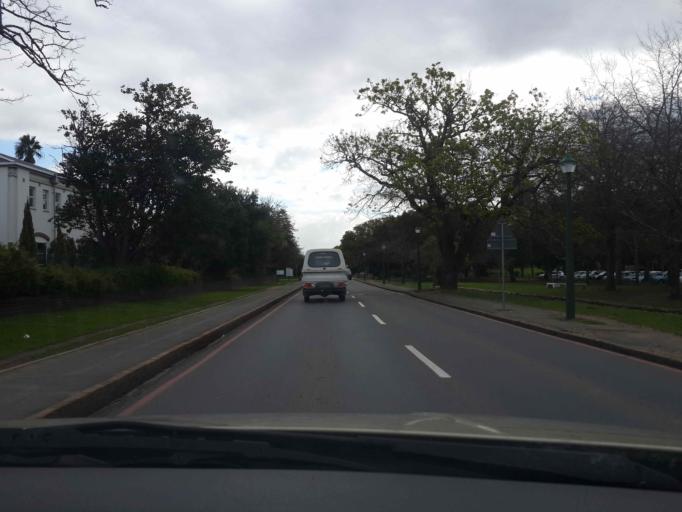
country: ZA
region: Western Cape
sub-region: Cape Winelands District Municipality
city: Stellenbosch
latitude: -33.9362
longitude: 18.8729
